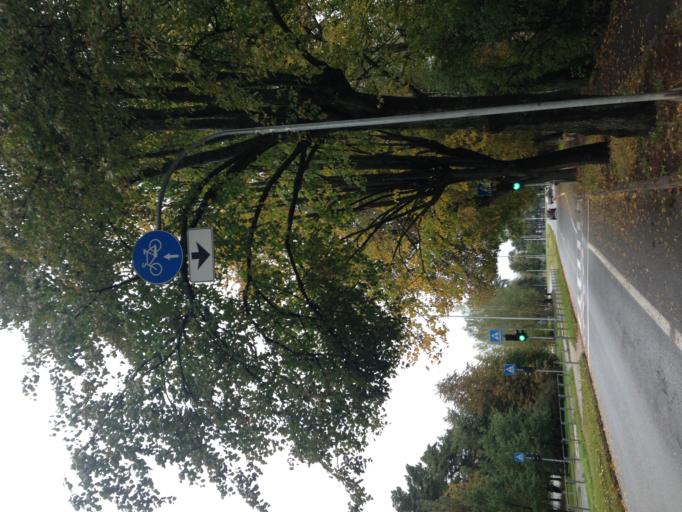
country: LV
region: Marupe
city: Marupe
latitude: 56.9552
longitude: 24.0238
